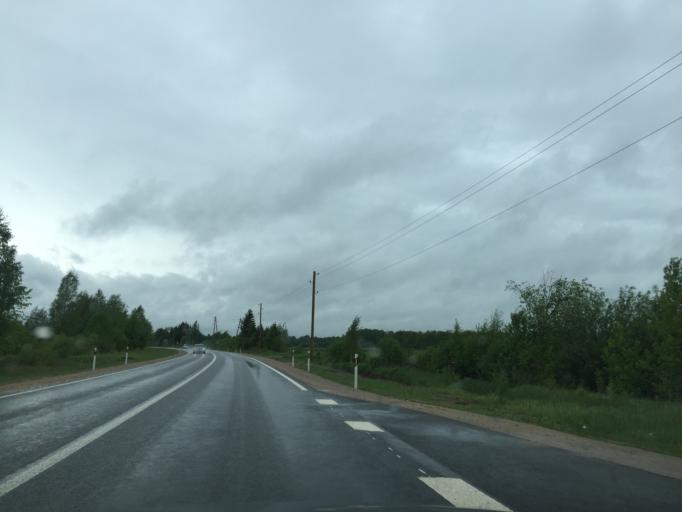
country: LV
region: Lielvarde
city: Lielvarde
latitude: 56.7015
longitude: 24.8818
